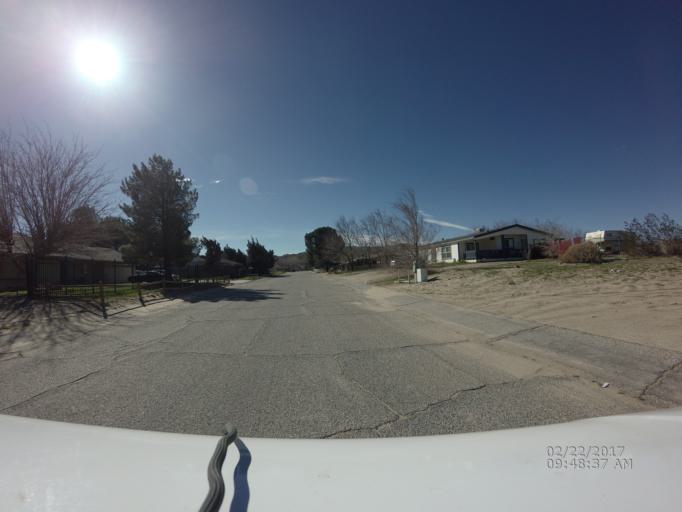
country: US
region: California
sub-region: Los Angeles County
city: Lake Los Angeles
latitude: 34.6214
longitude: -117.8431
